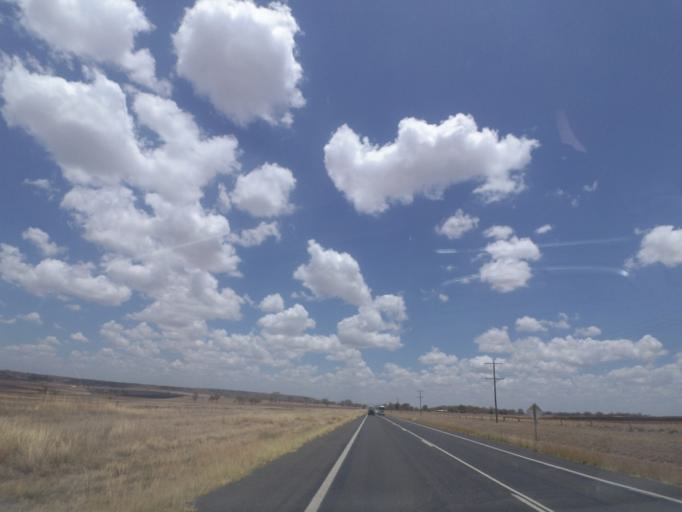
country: AU
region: Queensland
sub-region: Southern Downs
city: Warwick
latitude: -27.9856
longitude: 152.0007
